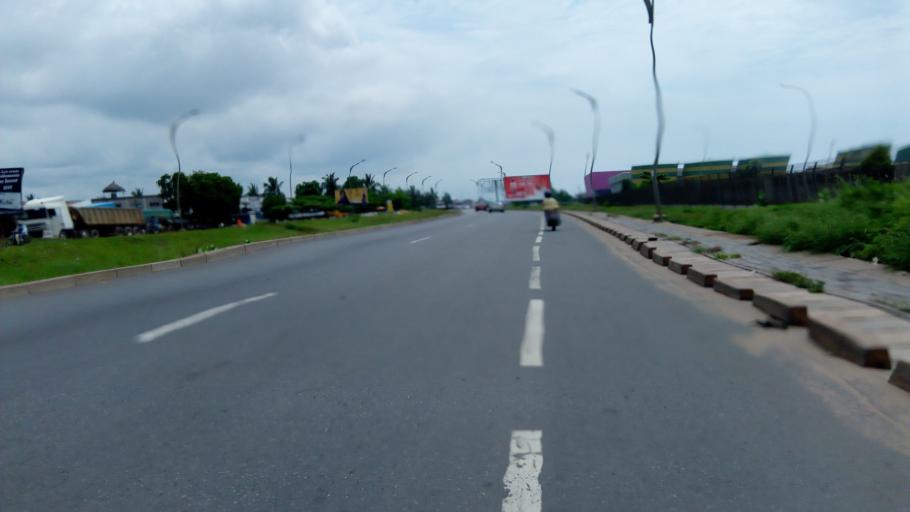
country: TG
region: Maritime
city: Lome
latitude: 6.1532
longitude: 1.2930
